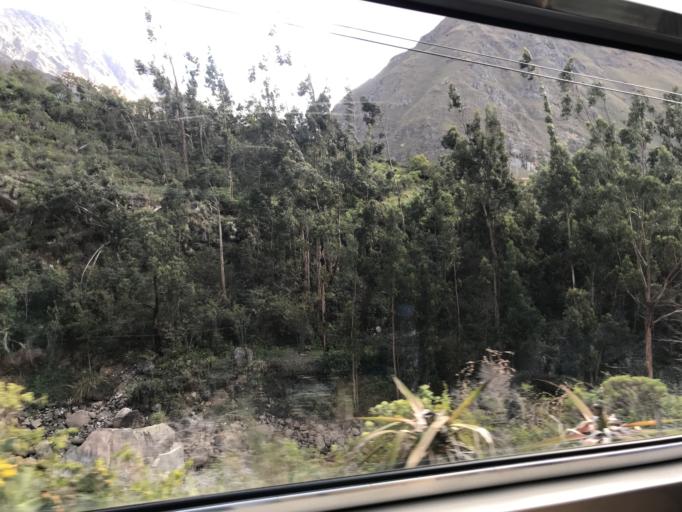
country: PE
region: Cusco
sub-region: Provincia de Urubamba
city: Ollantaytambo
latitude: -13.2258
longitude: -72.4225
